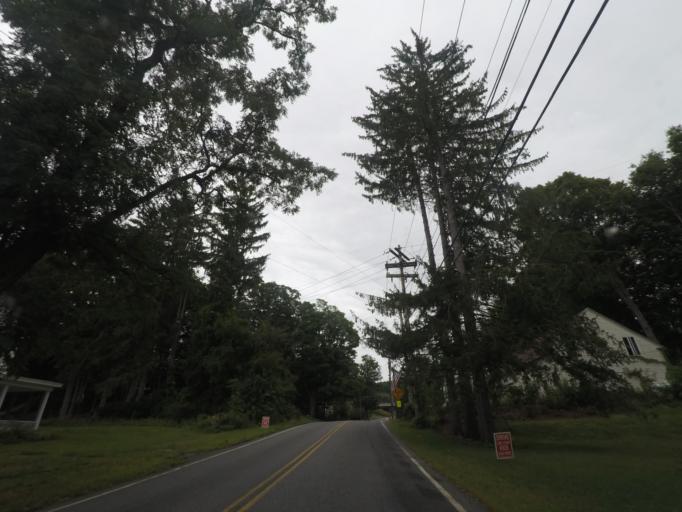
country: US
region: New York
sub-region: Columbia County
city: Chatham
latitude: 42.4406
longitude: -73.5589
